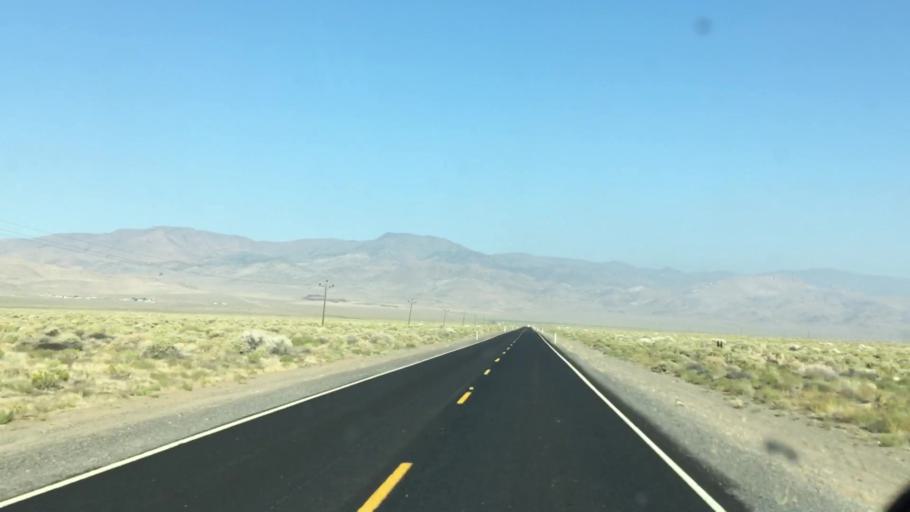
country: US
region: Nevada
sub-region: Lyon County
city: Fernley
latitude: 39.6455
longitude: -119.3109
